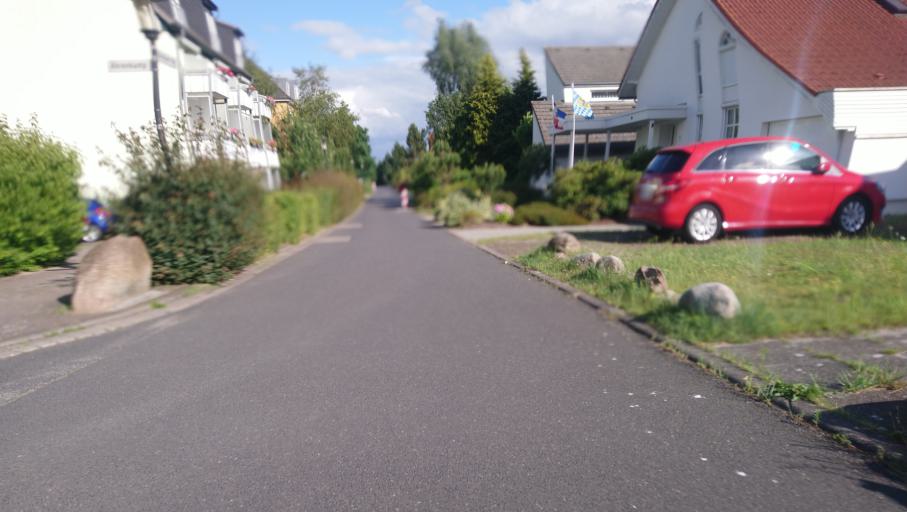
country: DE
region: Mecklenburg-Vorpommern
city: Papendorf
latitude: 54.0588
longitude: 12.1114
